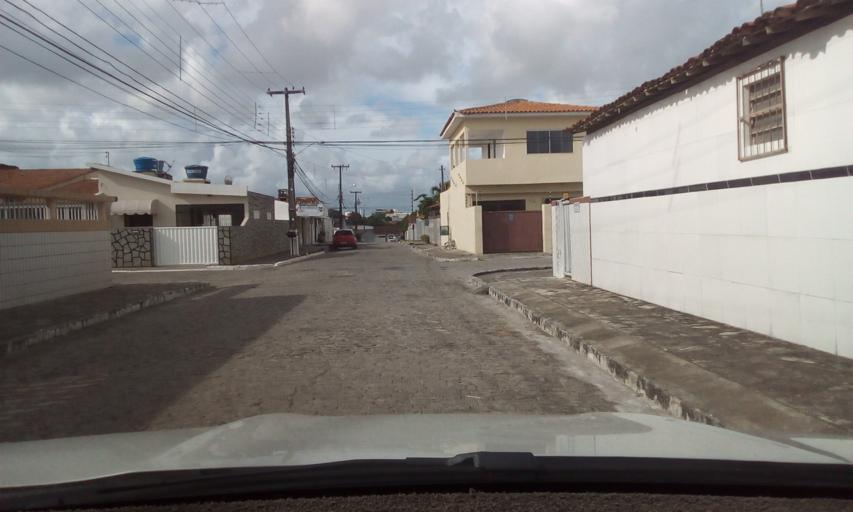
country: BR
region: Paraiba
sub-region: Joao Pessoa
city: Joao Pessoa
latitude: -7.1112
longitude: -34.8659
